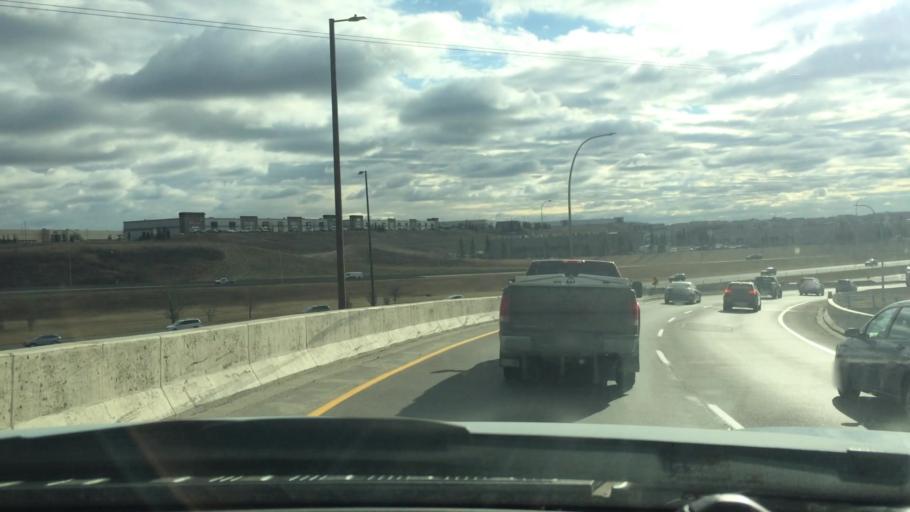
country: CA
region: Alberta
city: Calgary
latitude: 51.1250
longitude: -114.0474
